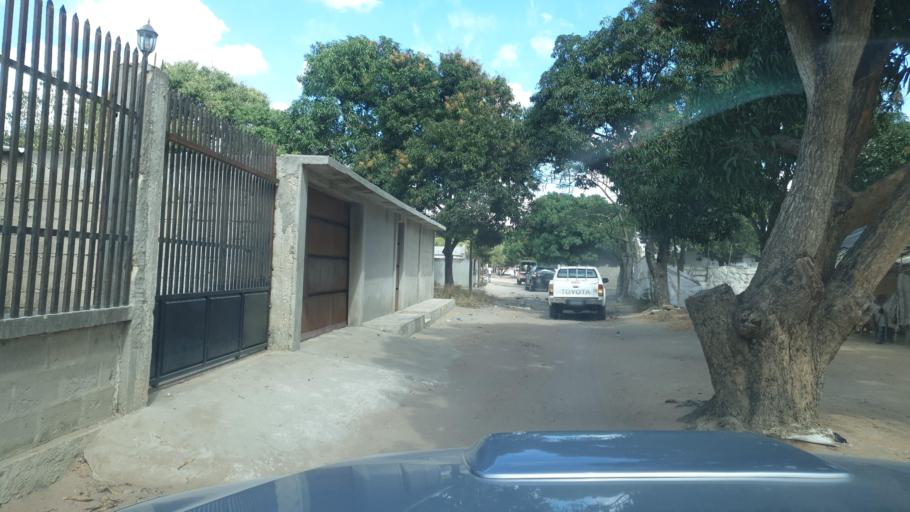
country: MZ
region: Nampula
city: Nacala
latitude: -14.5691
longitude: 40.6999
